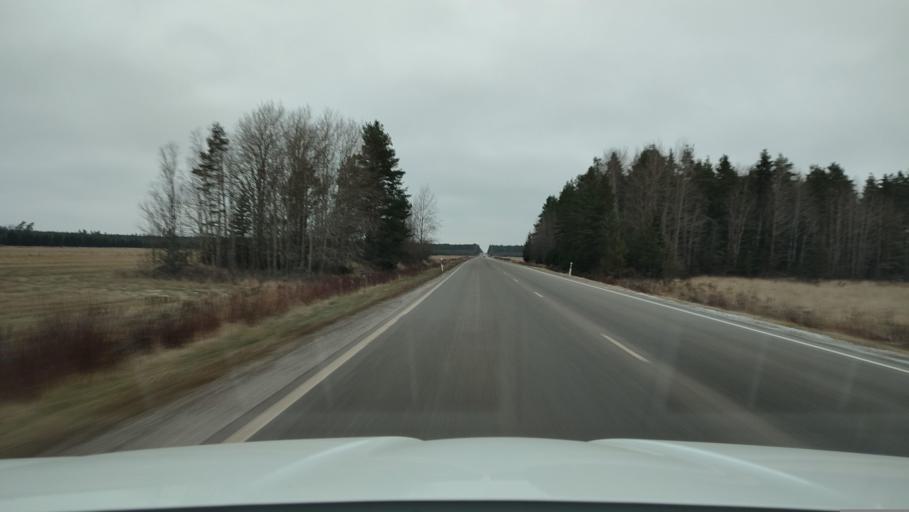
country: FI
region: Ostrobothnia
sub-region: Sydosterbotten
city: Naerpes
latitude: 62.4799
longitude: 21.4393
